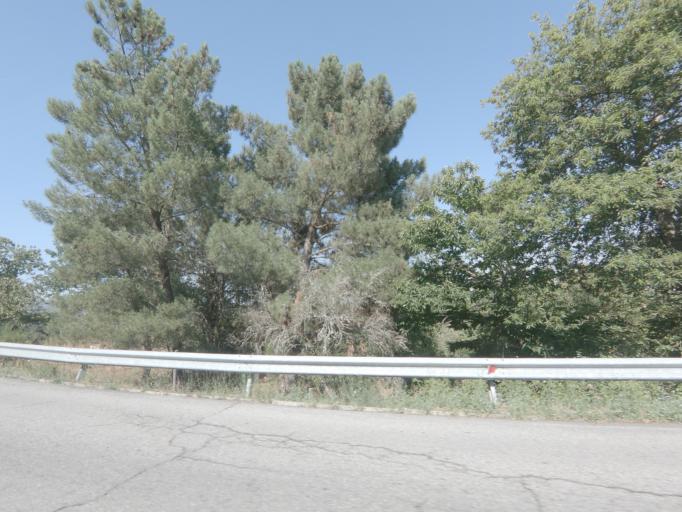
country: PT
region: Viseu
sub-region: Moimenta da Beira
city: Moimenta da Beira
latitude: 40.9787
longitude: -7.5989
